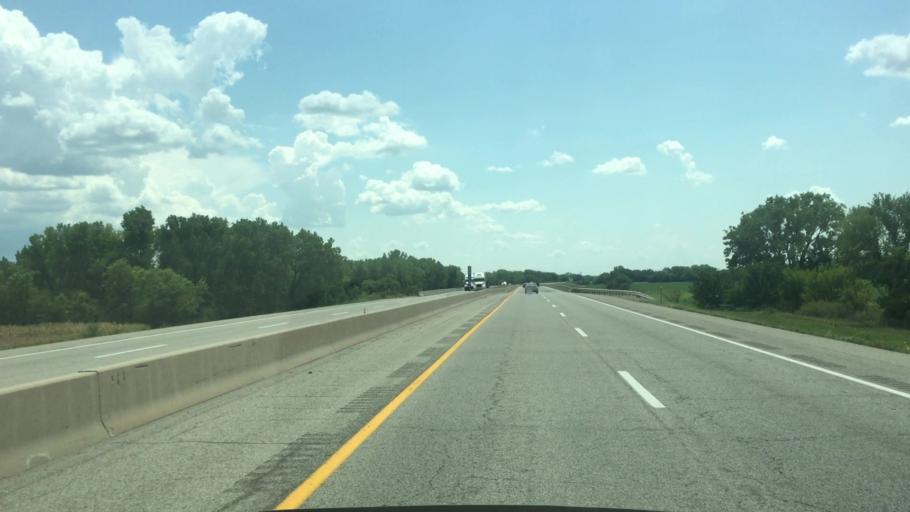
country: US
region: Kansas
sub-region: Lyon County
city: Emporia
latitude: 38.3962
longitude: -96.2510
